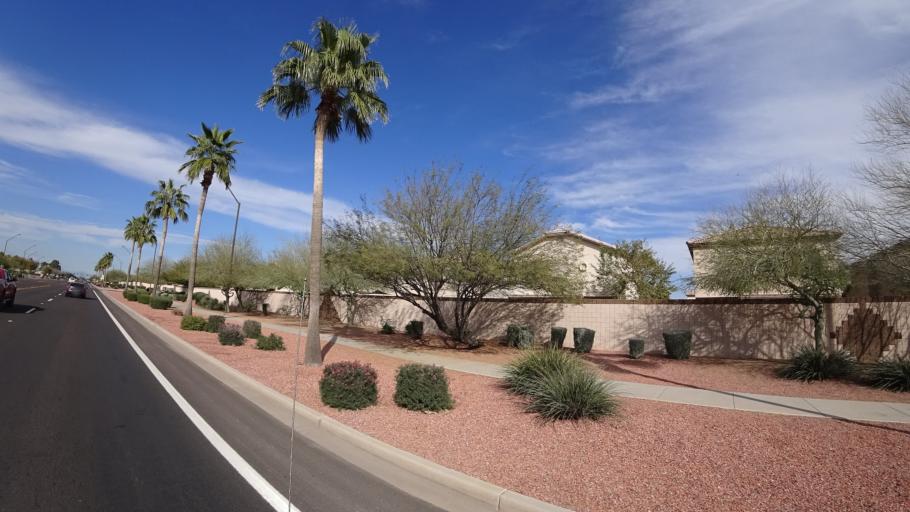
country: US
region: Arizona
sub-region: Maricopa County
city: Avondale
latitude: 33.4308
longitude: -112.3063
